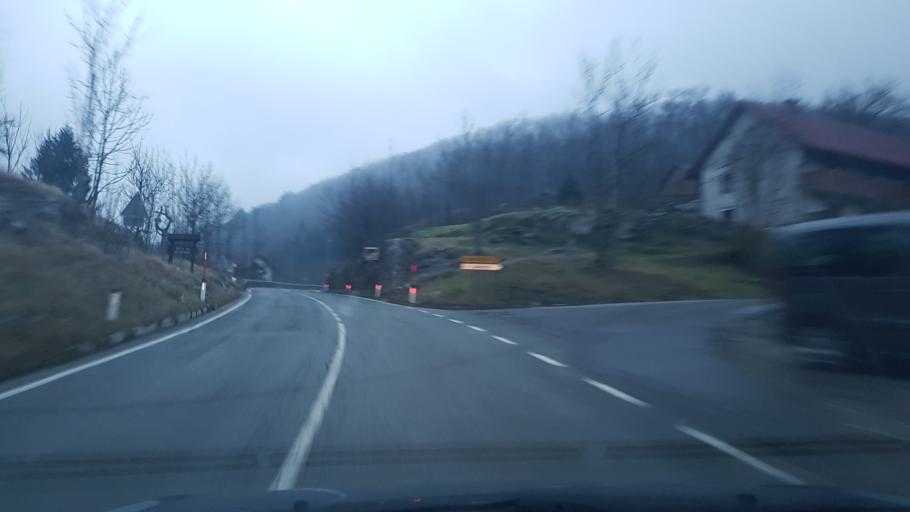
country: SI
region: Vipava
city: Vipava
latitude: 45.9085
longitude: 14.0233
